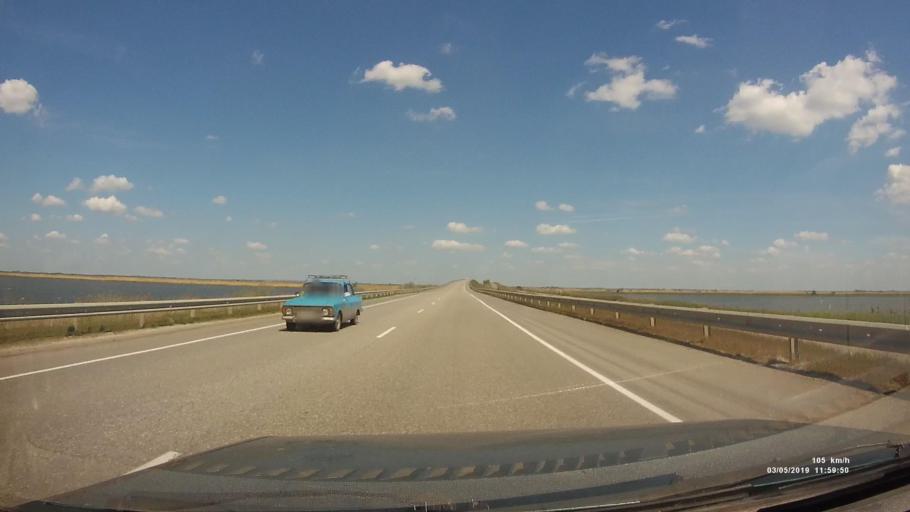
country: RU
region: Rostov
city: Bagayevskaya
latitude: 47.2404
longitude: 40.3342
